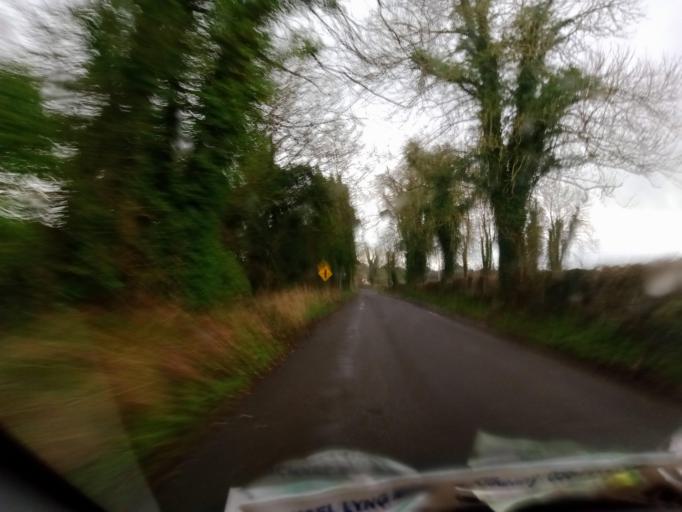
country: IE
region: Munster
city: Fethard
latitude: 52.5399
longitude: -7.7590
